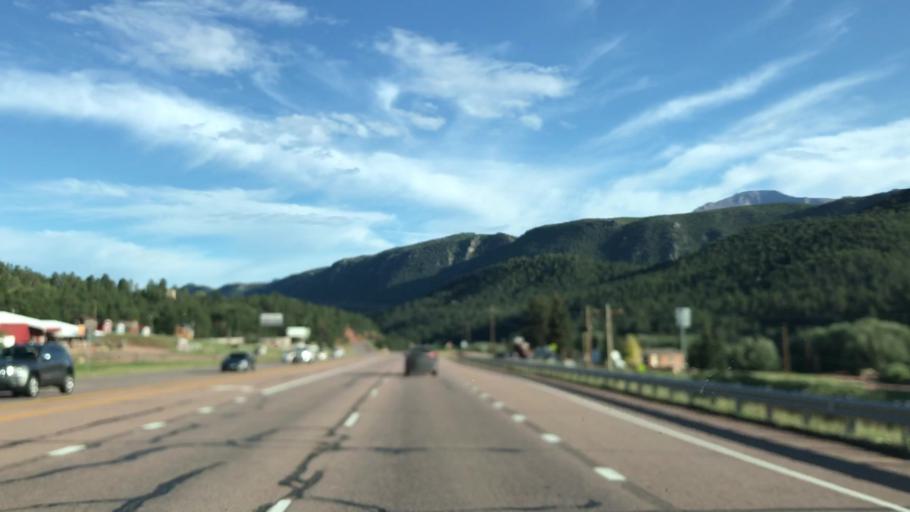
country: US
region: Colorado
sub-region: El Paso County
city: Cascade-Chipita Park
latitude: 38.9586
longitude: -105.0285
